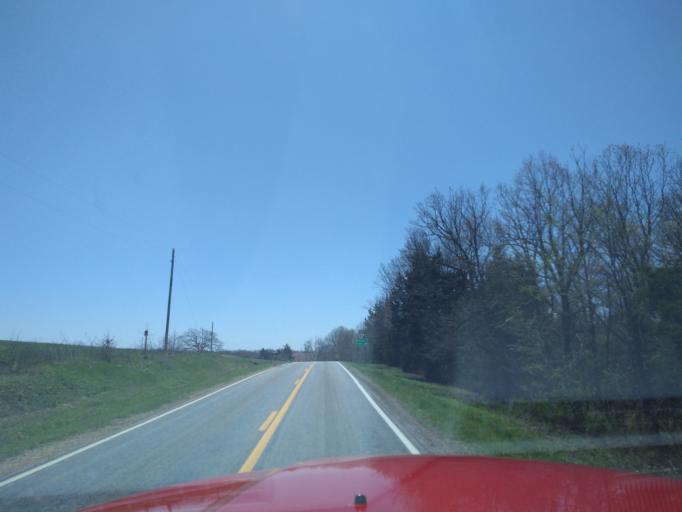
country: US
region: Arkansas
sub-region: Washington County
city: West Fork
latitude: 35.8456
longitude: -94.2760
